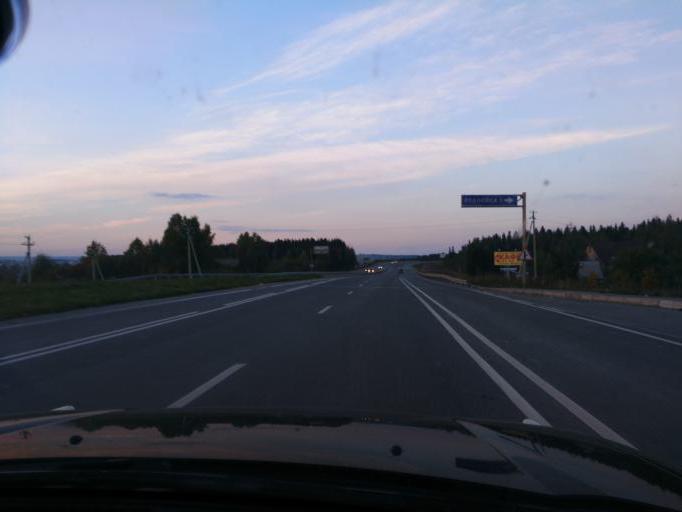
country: RU
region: Perm
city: Polazna
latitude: 58.2677
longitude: 56.4137
